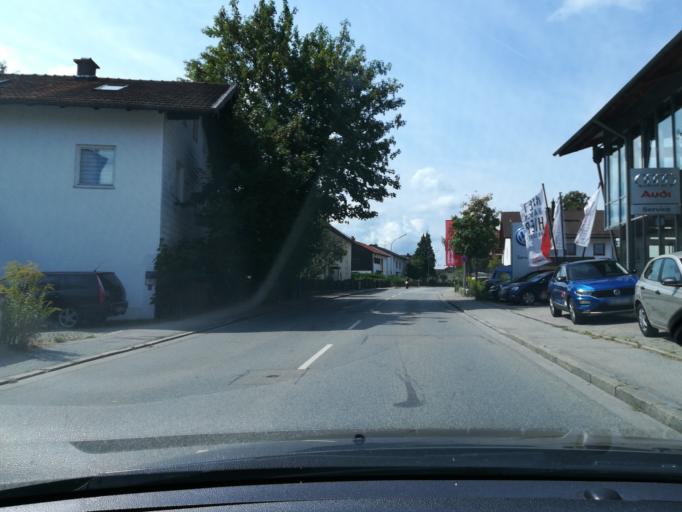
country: DE
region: Bavaria
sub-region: Upper Bavaria
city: Grafing bei Munchen
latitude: 48.0437
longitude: 11.9638
